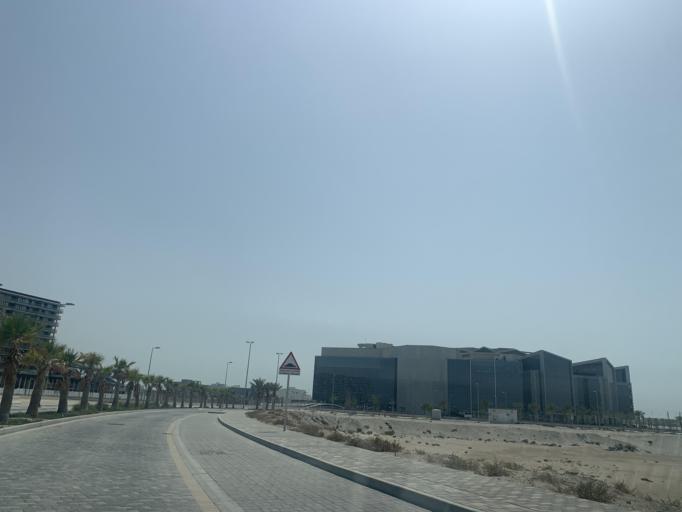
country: BH
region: Muharraq
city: Al Hadd
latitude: 26.2714
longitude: 50.6755
